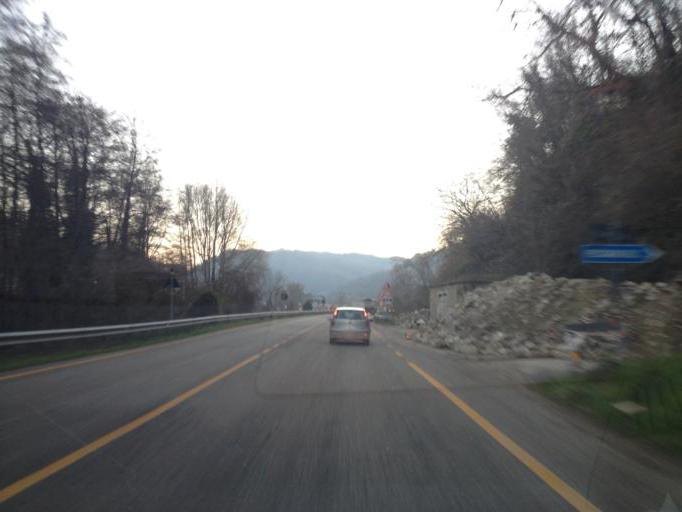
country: IT
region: The Marches
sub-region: Provincia di Ascoli Piceno
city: Arquata del Tronto
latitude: 42.7485
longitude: 13.2708
